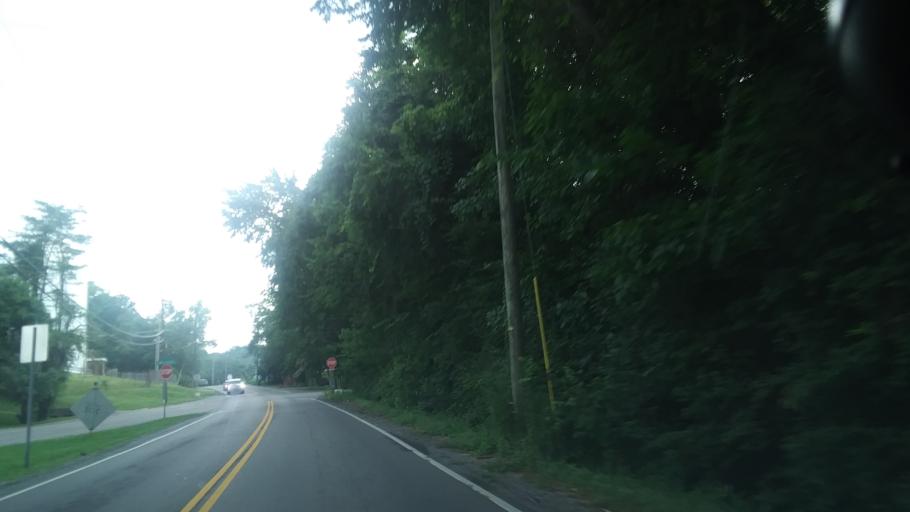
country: US
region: Tennessee
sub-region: Davidson County
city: Belle Meade
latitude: 36.0886
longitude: -86.9354
